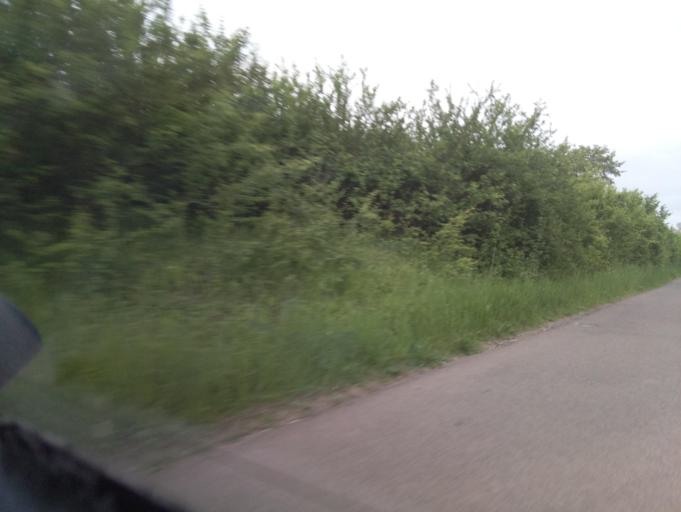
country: GB
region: England
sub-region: South Gloucestershire
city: Pucklechurch
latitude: 51.4640
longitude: -2.4203
